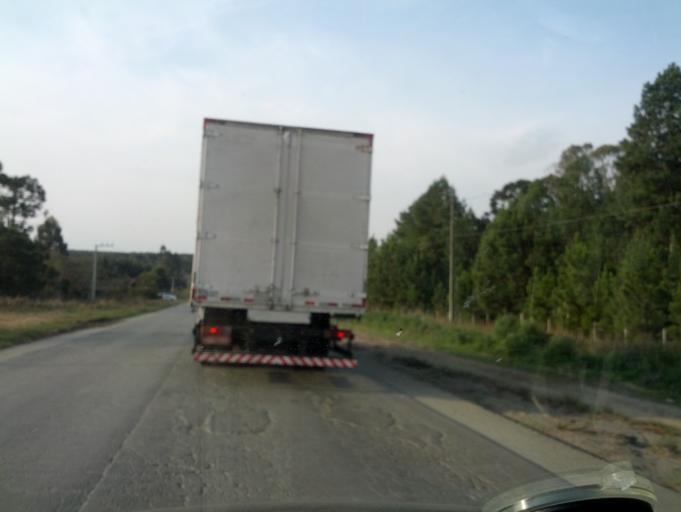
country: BR
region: Santa Catarina
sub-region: Otacilio Costa
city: Otacilio Costa
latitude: -27.5209
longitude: -50.1349
